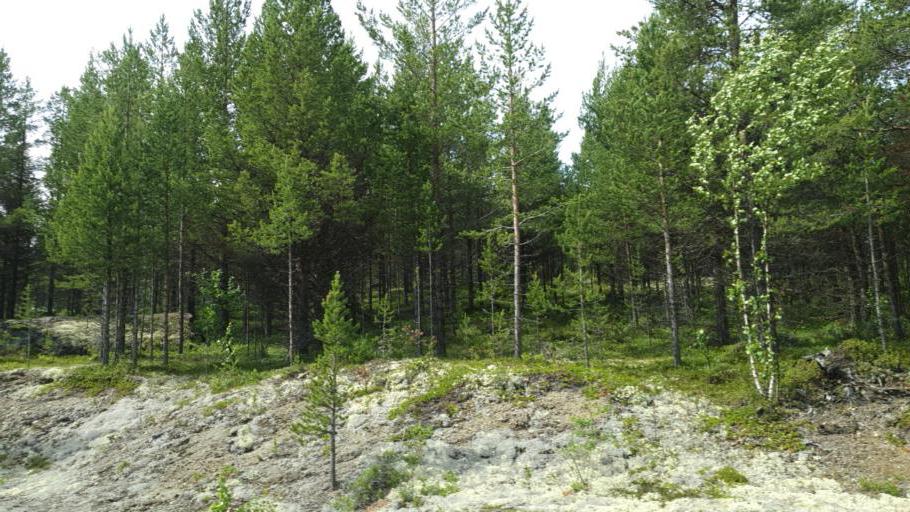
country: NO
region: Oppland
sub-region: Vaga
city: Vagamo
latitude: 61.6855
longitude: 9.0588
